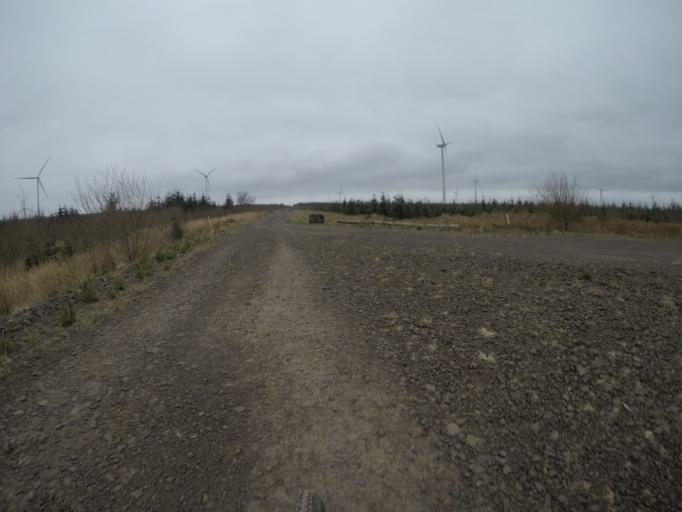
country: GB
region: Scotland
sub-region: East Ayrshire
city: Newmilns
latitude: 55.6577
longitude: -4.3294
